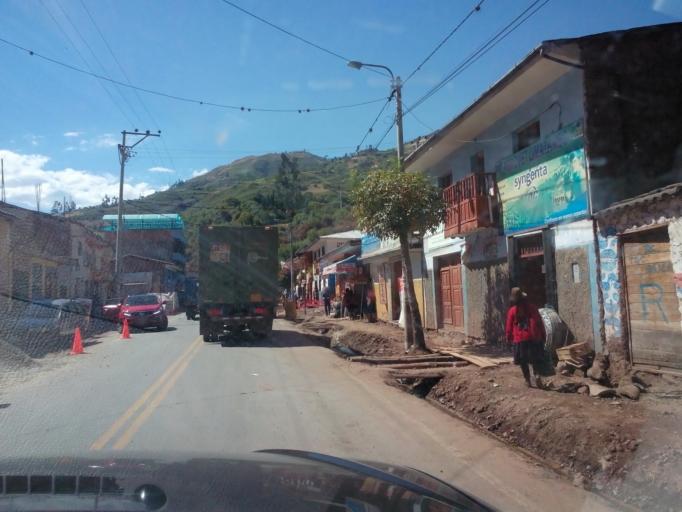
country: PE
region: Cusco
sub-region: Provincia de Anta
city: Limatambo
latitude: -13.4789
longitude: -72.4443
